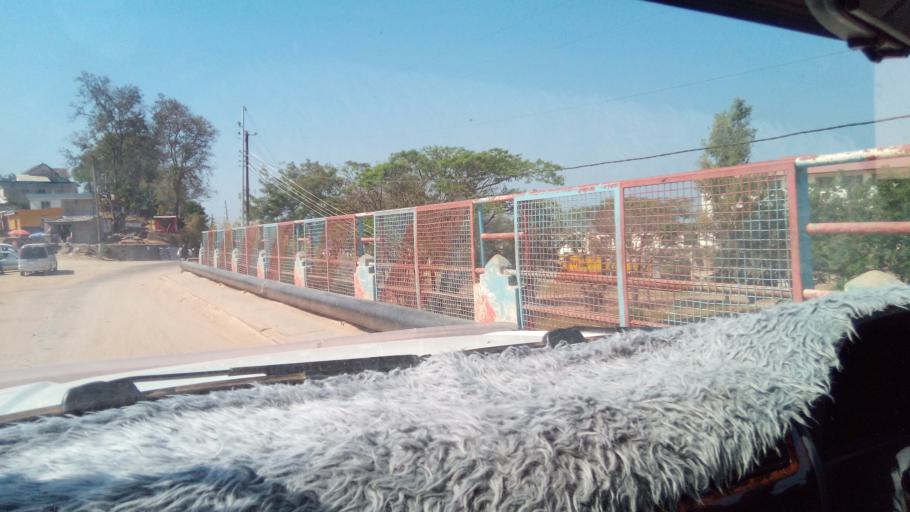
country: CD
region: Katanga
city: Kalemie
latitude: -5.9476
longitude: 29.1966
